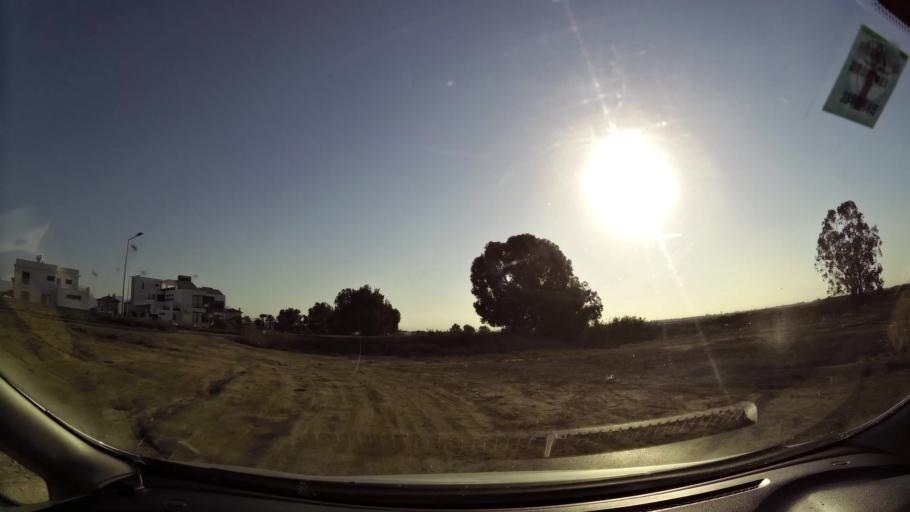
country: CY
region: Lefkosia
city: Nicosia
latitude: 35.2008
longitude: 33.2950
